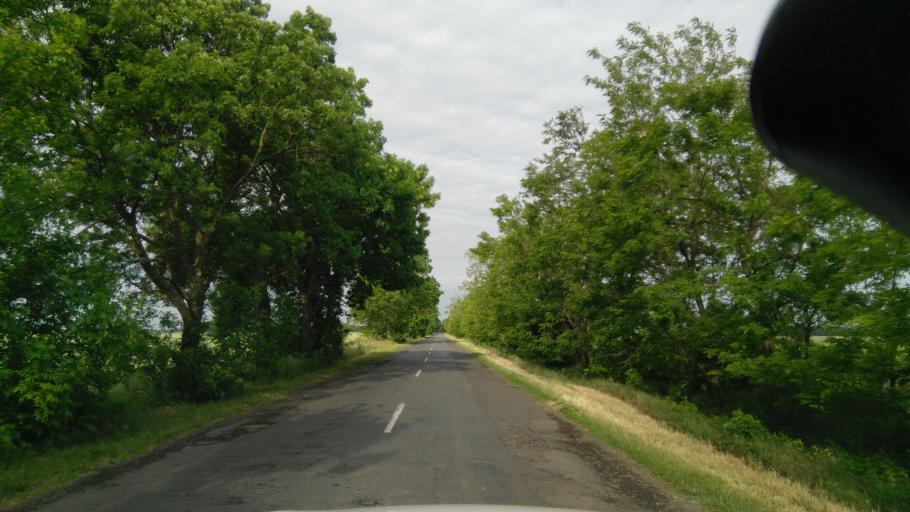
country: HU
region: Bekes
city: Medgyesegyhaza
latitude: 46.5292
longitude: 21.0981
